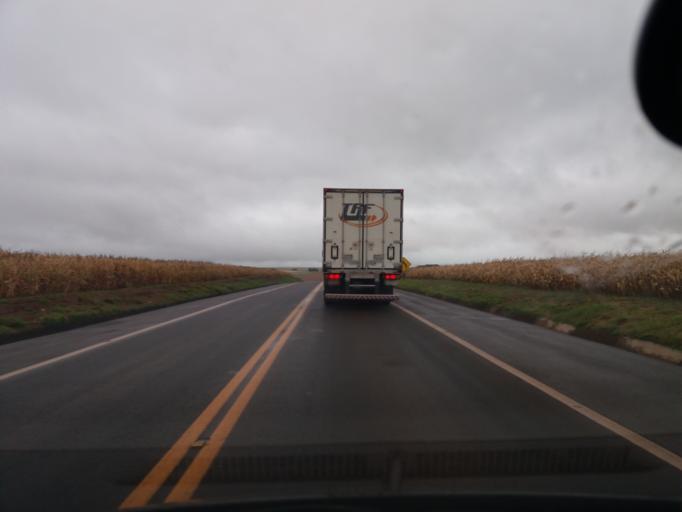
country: BR
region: Parana
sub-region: Campo Mourao
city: Campo Mourao
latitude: -24.3327
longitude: -52.6643
